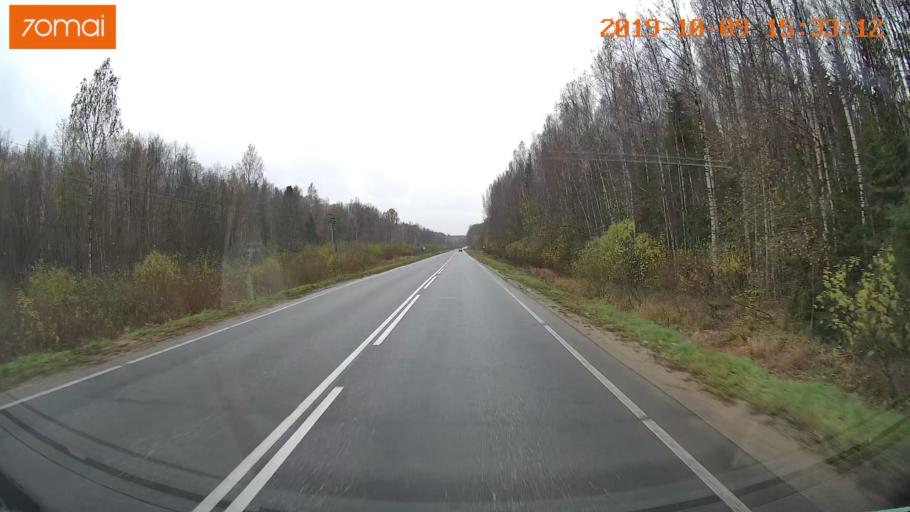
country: RU
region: Kostroma
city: Oktyabr'skiy
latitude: 57.9549
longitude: 41.2656
